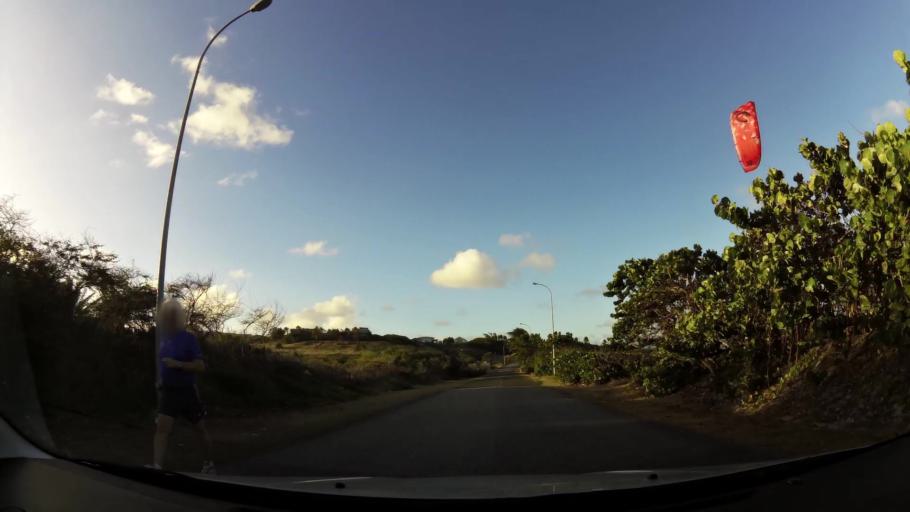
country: AG
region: Saint George
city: Piggotts
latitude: 17.1640
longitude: -61.8001
